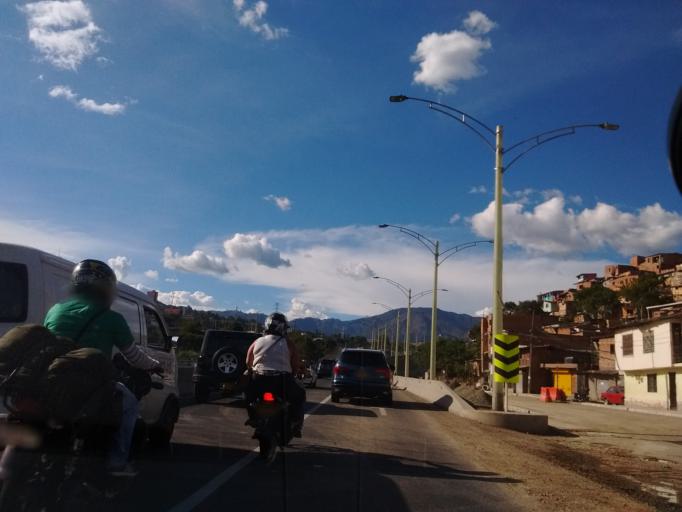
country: CO
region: Antioquia
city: Medellin
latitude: 6.2815
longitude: -75.5680
